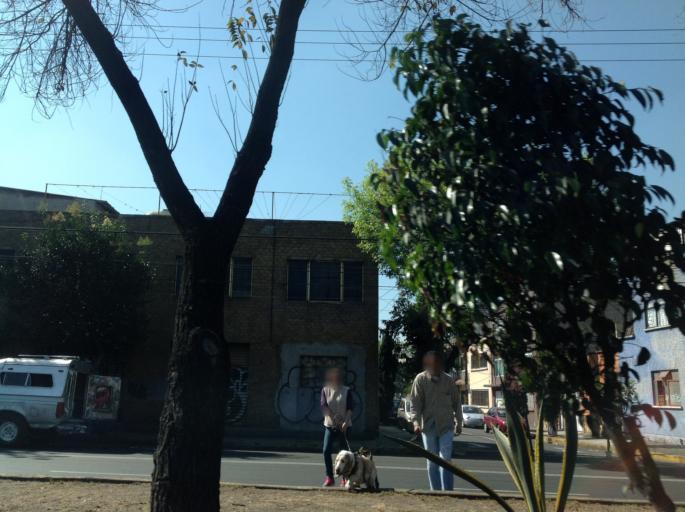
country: MX
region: Mexico City
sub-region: Iztacalco
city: Iztacalco
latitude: 19.4184
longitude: -99.0946
